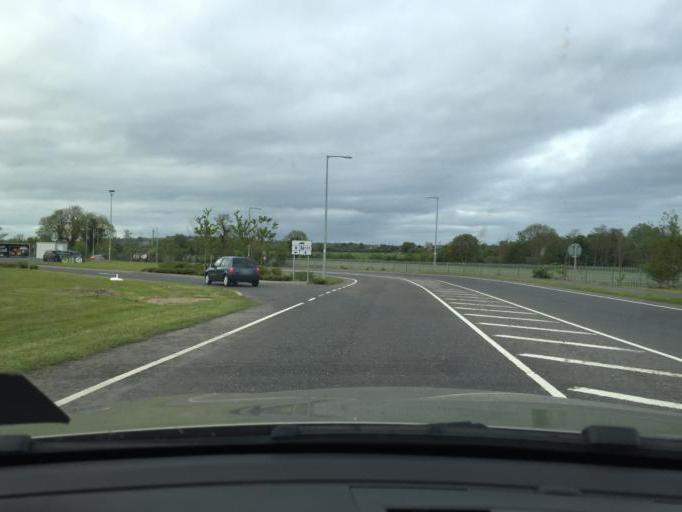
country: IE
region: Leinster
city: Lusk
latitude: 53.5396
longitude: -6.2091
